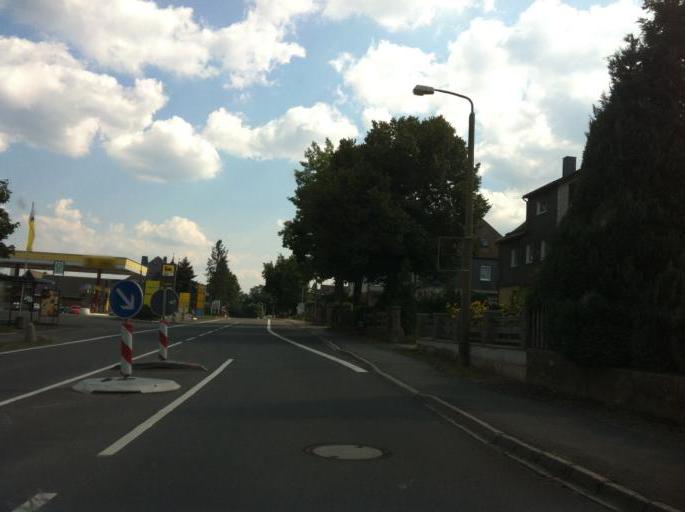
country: DE
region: Thuringia
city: Grossbreitenbach
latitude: 50.5830
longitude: 10.9966
